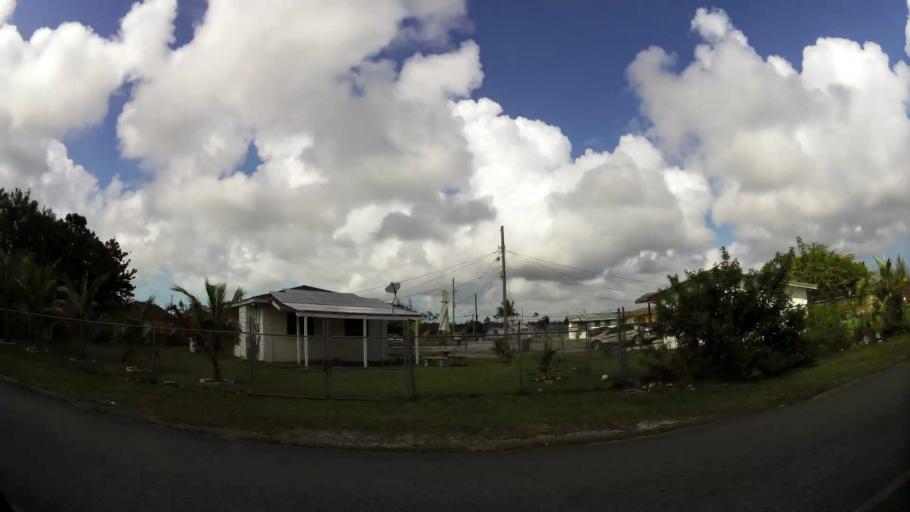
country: BS
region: Freeport
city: Lucaya
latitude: 26.5342
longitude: -78.6704
